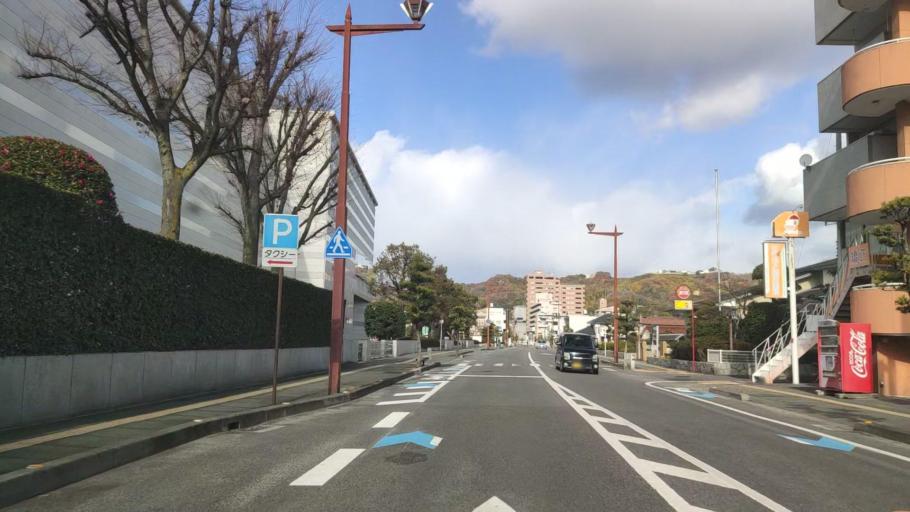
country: JP
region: Ehime
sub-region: Shikoku-chuo Shi
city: Matsuyama
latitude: 33.8482
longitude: 132.7805
